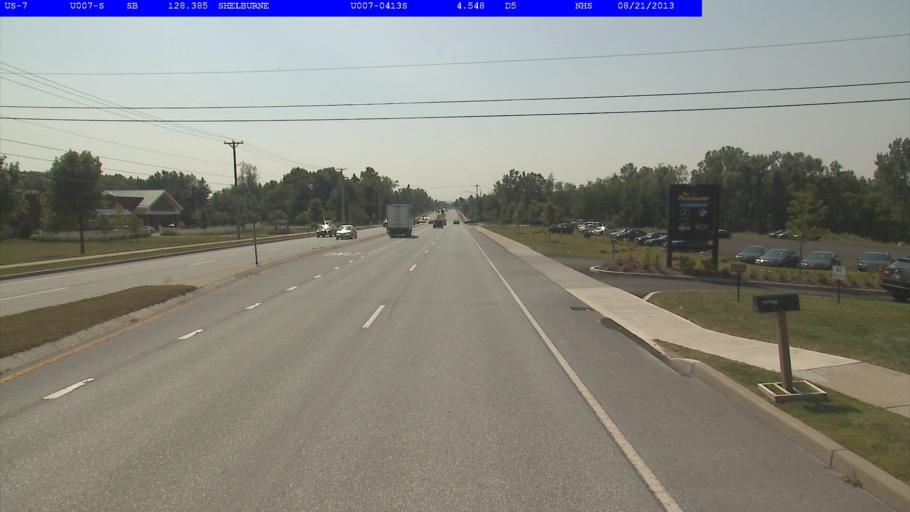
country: US
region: Vermont
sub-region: Chittenden County
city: Burlington
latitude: 44.4077
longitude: -73.2163
